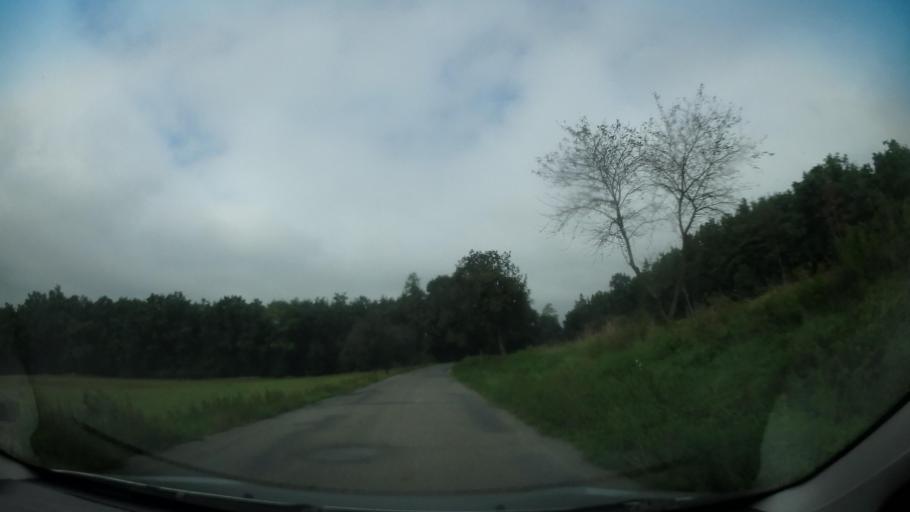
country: CZ
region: Central Bohemia
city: Sedlcany
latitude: 49.7102
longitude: 14.4242
